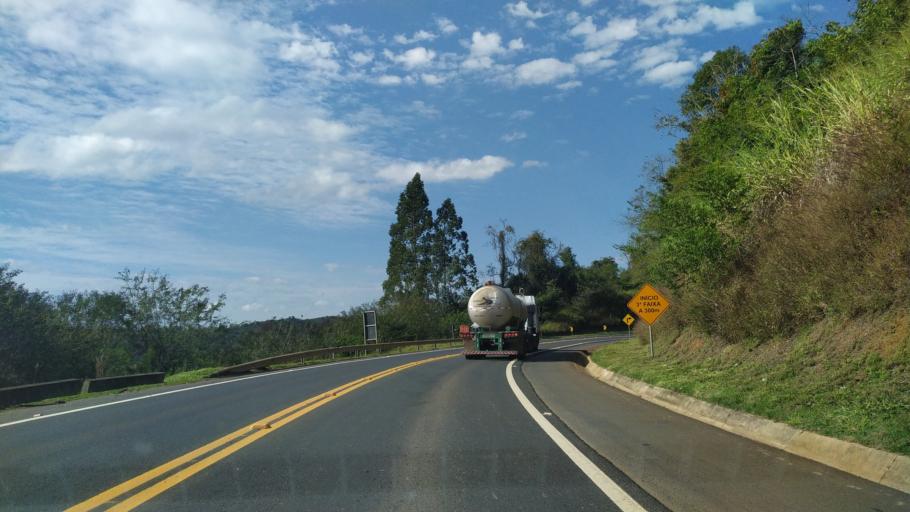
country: BR
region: Parana
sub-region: Telemaco Borba
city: Telemaco Borba
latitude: -24.2717
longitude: -50.7166
